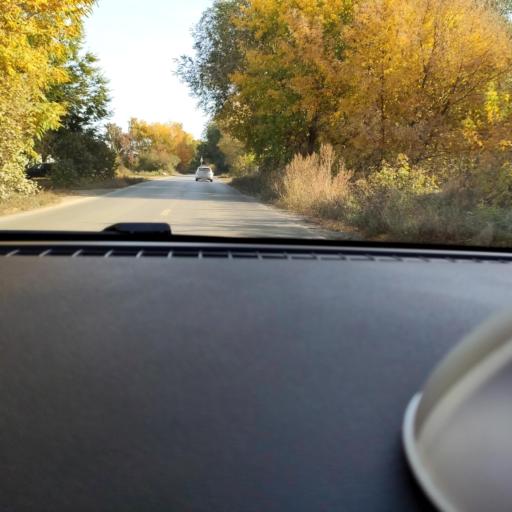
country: RU
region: Samara
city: Smyshlyayevka
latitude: 53.2383
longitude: 50.3395
